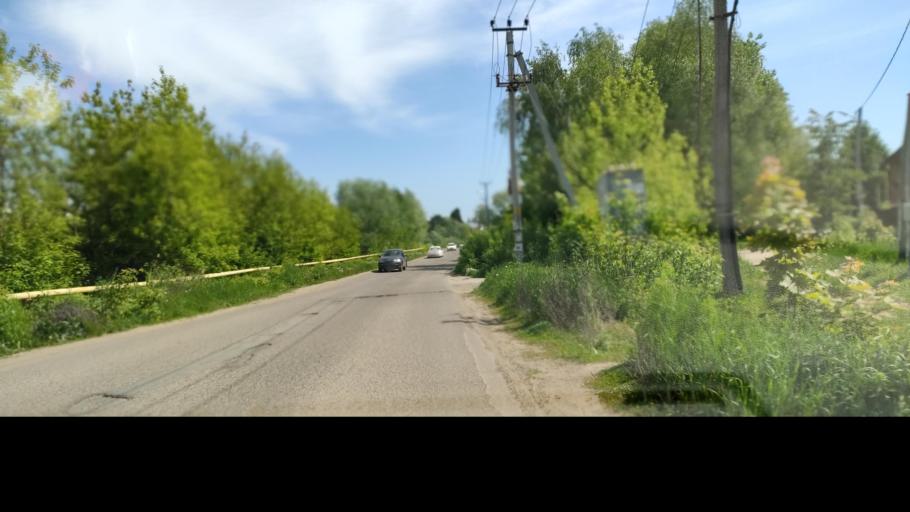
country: RU
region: Tatarstan
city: Osinovo
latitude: 55.8310
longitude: 48.7902
